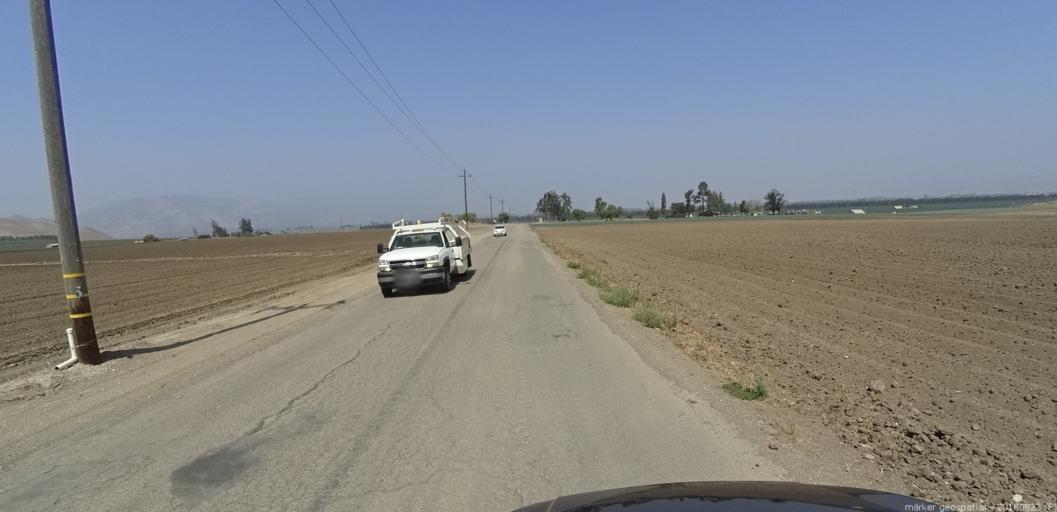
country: US
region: California
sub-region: Monterey County
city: Greenfield
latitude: 36.2835
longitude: -121.2352
